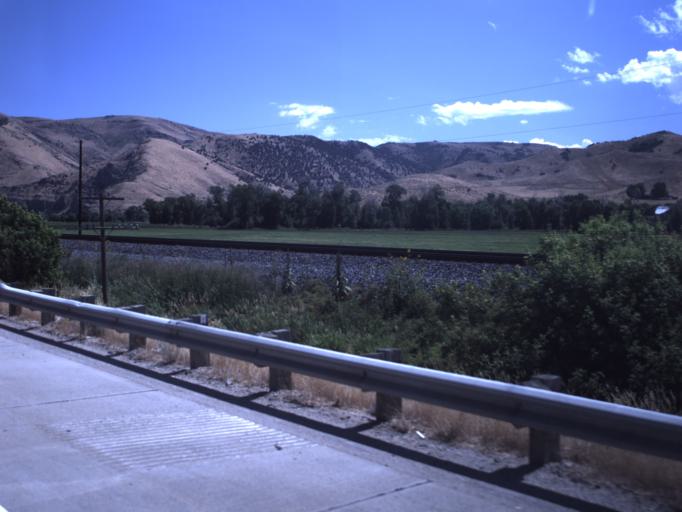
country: US
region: Utah
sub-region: Morgan County
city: Morgan
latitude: 41.0489
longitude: -111.6370
